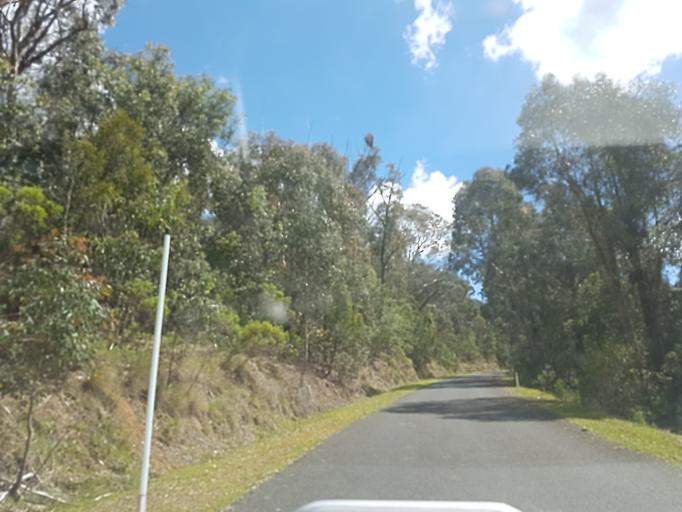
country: AU
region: Victoria
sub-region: East Gippsland
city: Bairnsdale
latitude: -37.4076
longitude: 147.2488
